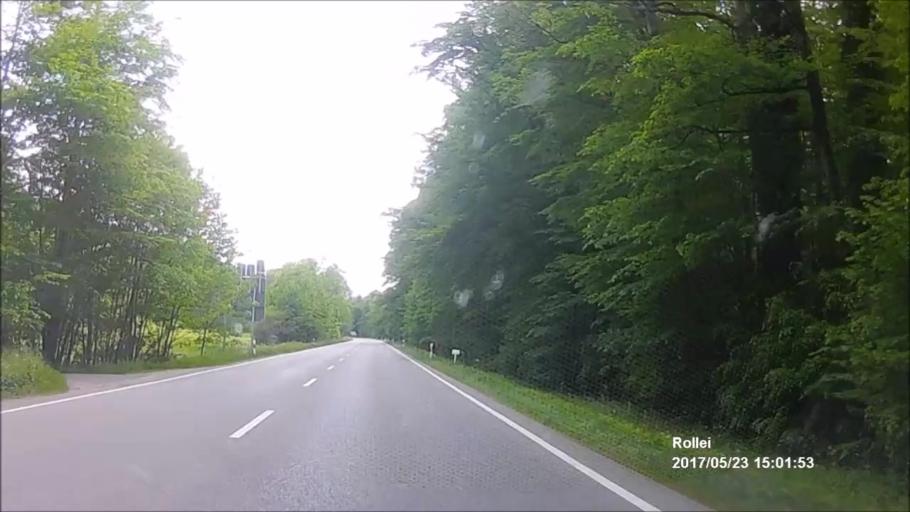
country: DE
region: Bavaria
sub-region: Upper Bavaria
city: Traunstein
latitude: 47.8537
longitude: 12.6386
